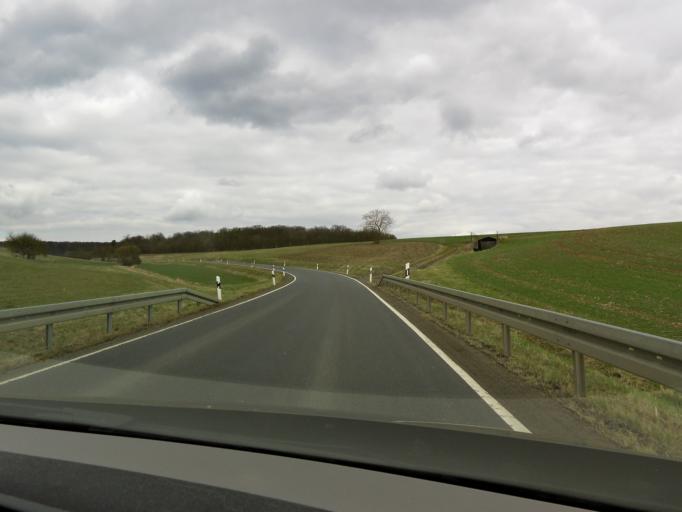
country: DE
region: Bavaria
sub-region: Regierungsbezirk Unterfranken
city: Rimpar
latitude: 49.8633
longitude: 9.9671
